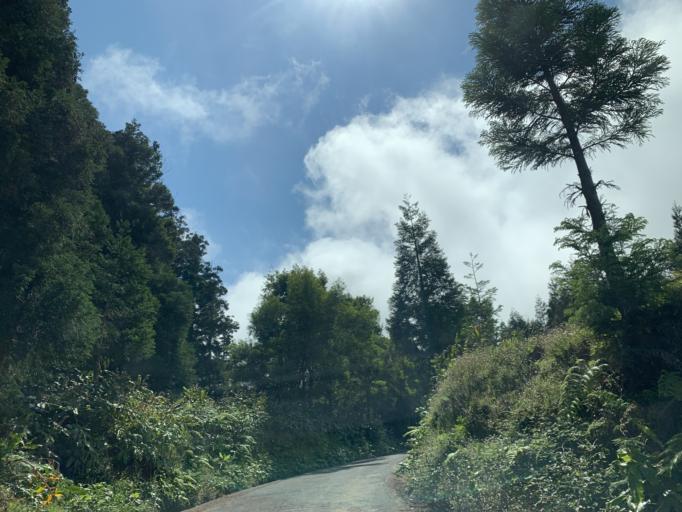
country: PT
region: Azores
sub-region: Ponta Delgada
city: Arrifes
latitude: 37.8506
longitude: -25.7348
